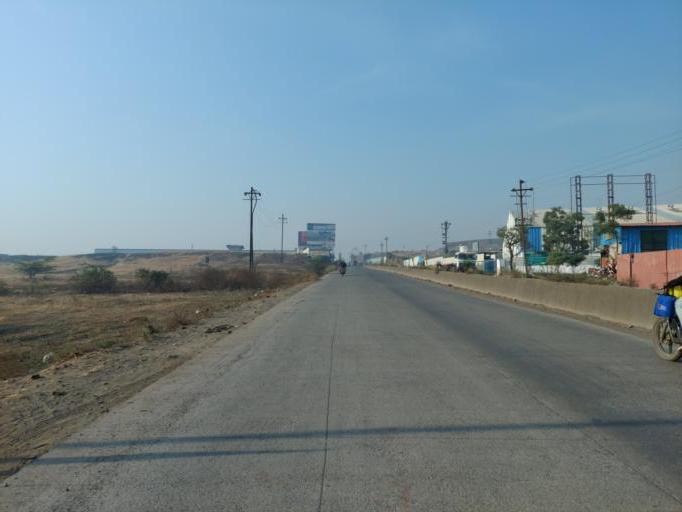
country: IN
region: Maharashtra
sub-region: Pune Division
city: Pune
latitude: 18.4616
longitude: 73.9504
